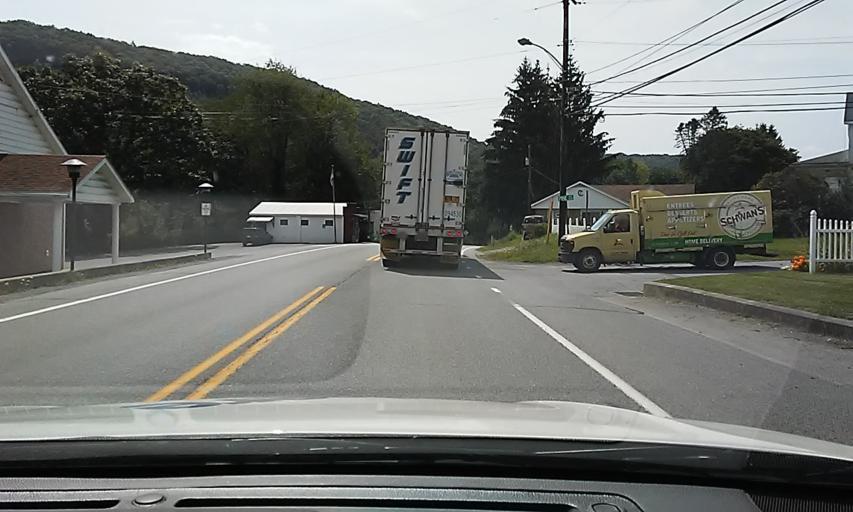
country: US
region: Pennsylvania
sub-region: Elk County
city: Saint Marys
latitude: 41.2580
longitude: -78.5015
